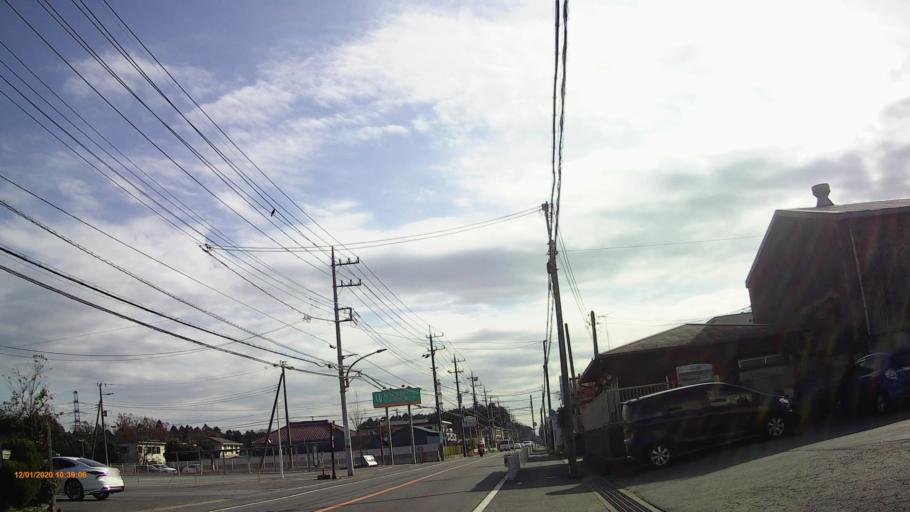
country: JP
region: Chiba
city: Yotsukaido
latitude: 35.6333
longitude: 140.1797
